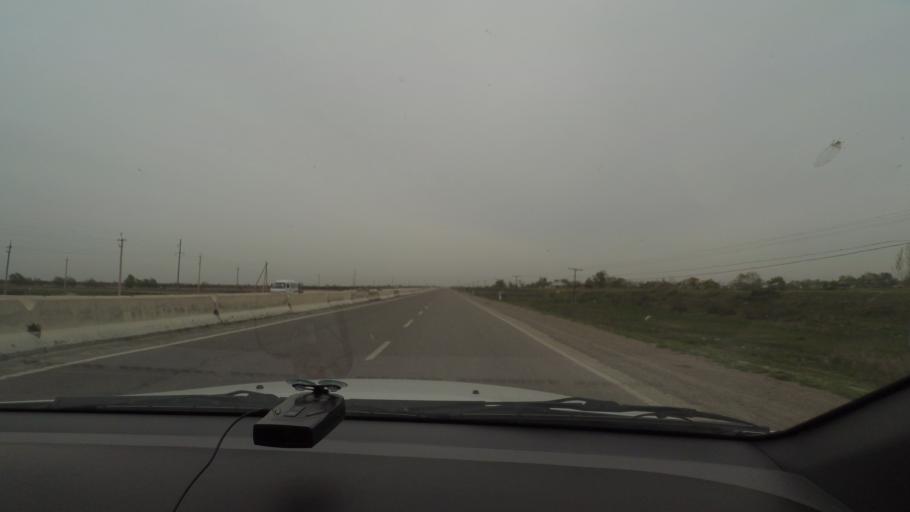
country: UZ
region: Sirdaryo
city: Guliston
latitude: 40.4946
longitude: 68.6504
